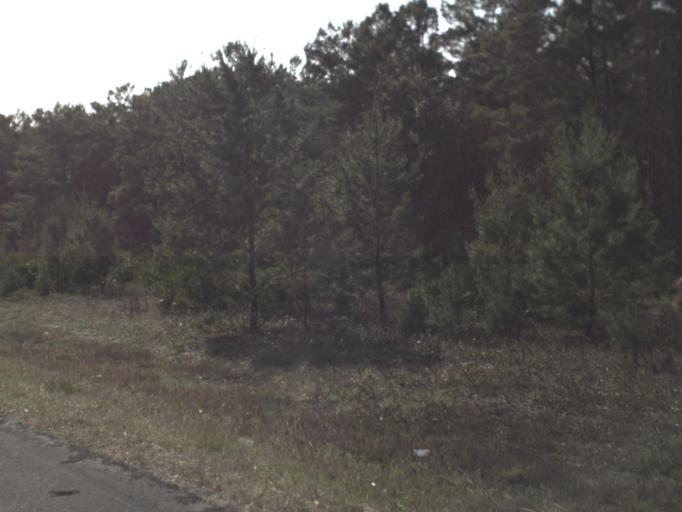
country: US
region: Florida
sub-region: Franklin County
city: Carrabelle
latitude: 29.9315
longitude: -84.5118
